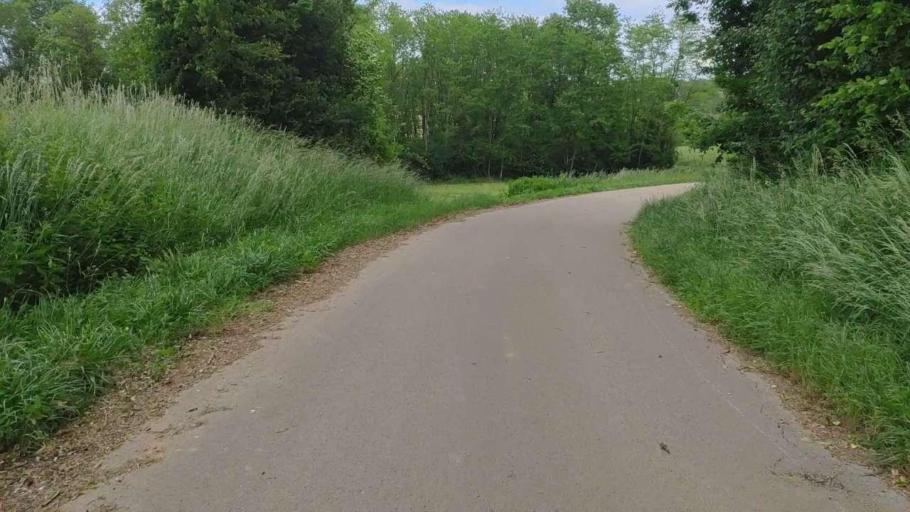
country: FR
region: Franche-Comte
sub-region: Departement du Jura
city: Bletterans
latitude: 46.7873
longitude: 5.5466
